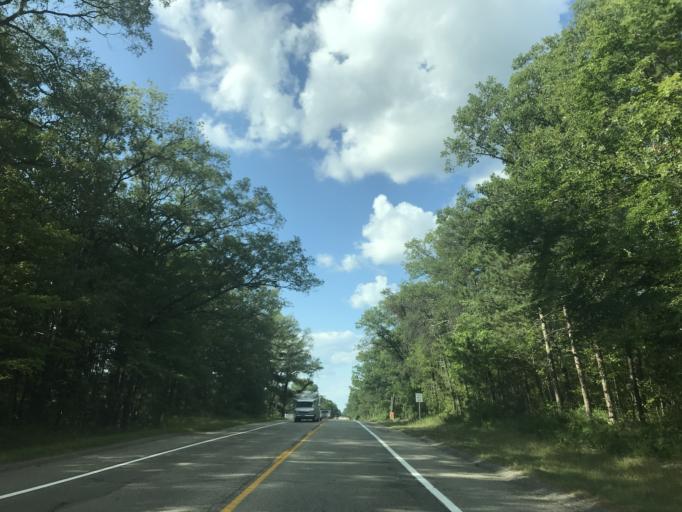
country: US
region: Michigan
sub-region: Newaygo County
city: White Cloud
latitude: 43.5170
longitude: -85.7720
